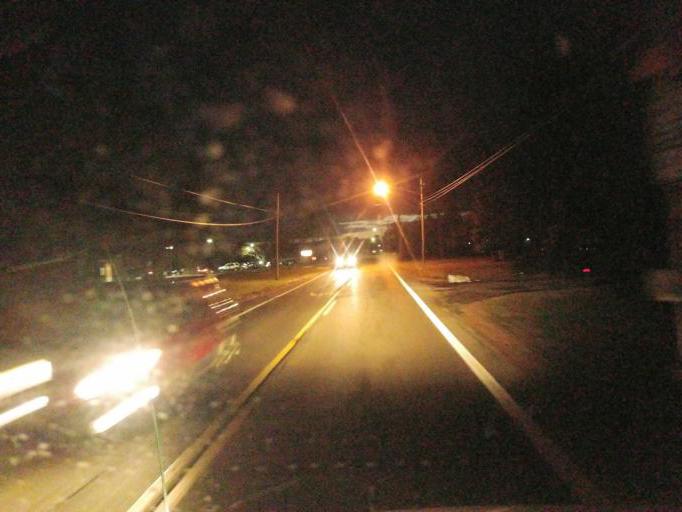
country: US
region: Ohio
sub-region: Morrow County
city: Cardington
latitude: 40.4953
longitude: -82.8808
